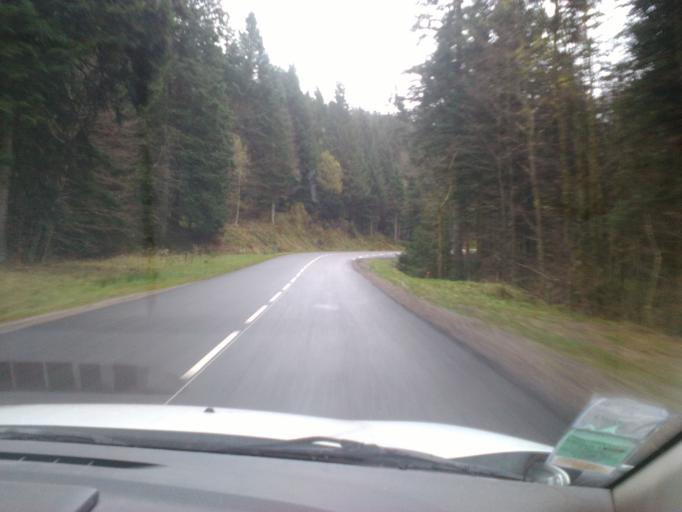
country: FR
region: Lorraine
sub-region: Departement des Vosges
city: Xonrupt-Longemer
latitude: 48.0547
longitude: 6.9880
